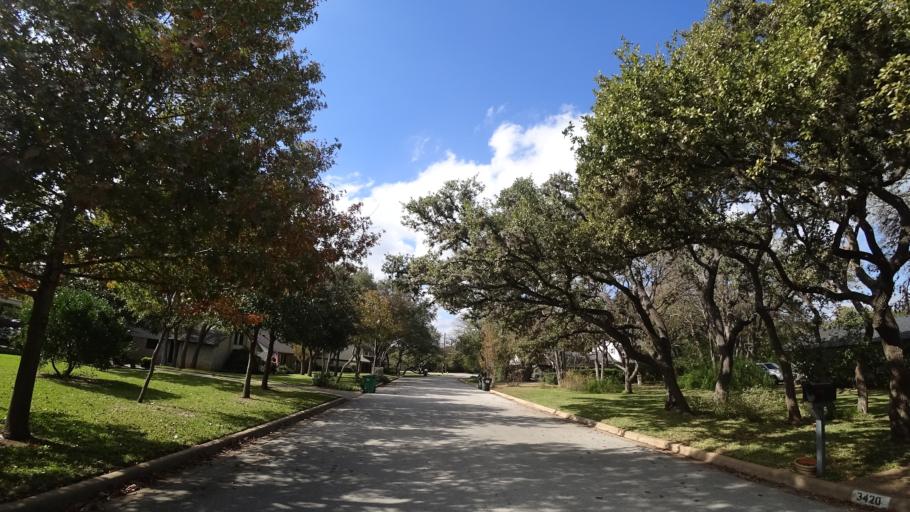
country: US
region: Texas
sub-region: Travis County
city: Shady Hollow
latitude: 30.1696
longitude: -97.8583
